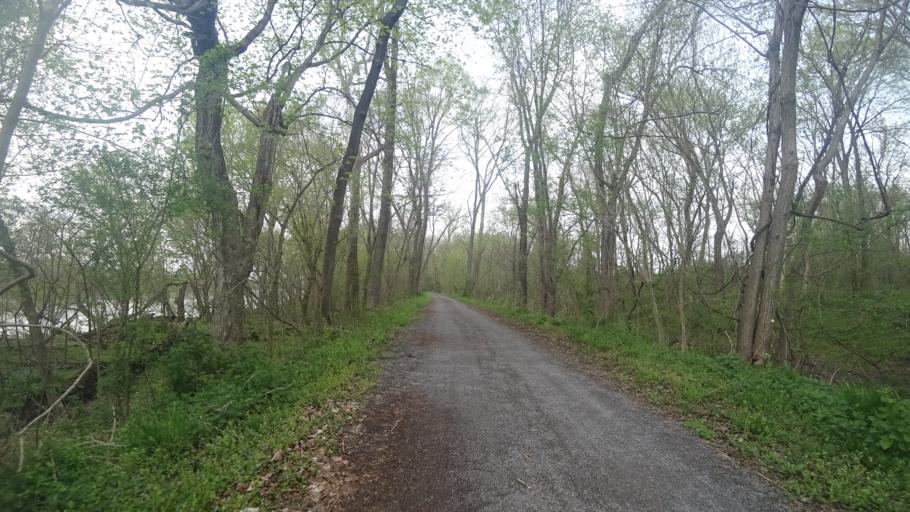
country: US
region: Virginia
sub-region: Loudoun County
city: Leesburg
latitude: 39.1327
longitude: -77.5144
